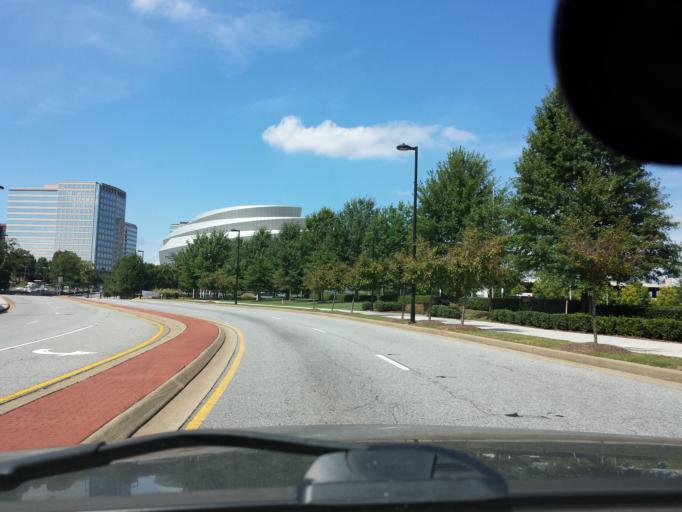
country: US
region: Georgia
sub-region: Cobb County
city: Vinings
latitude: 33.8828
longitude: -84.4575
